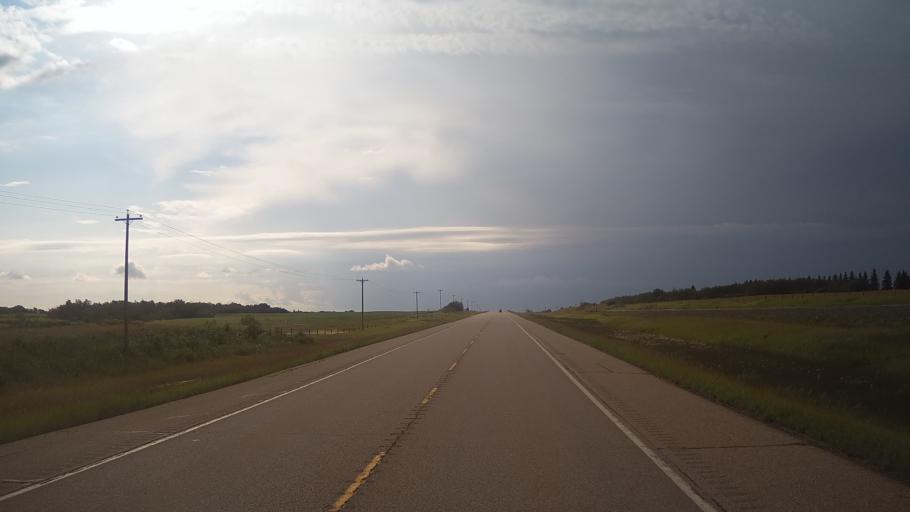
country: CA
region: Alberta
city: Viking
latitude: 53.1592
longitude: -111.9993
